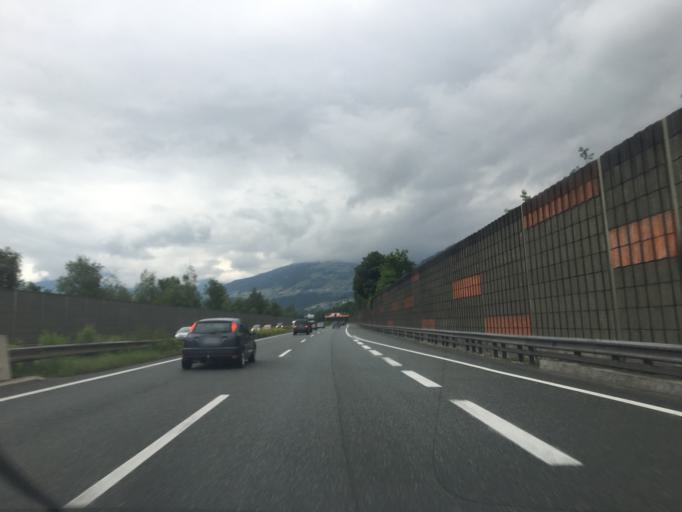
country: AT
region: Tyrol
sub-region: Politischer Bezirk Innsbruck Land
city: Fritzens
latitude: 47.3000
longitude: 11.5890
